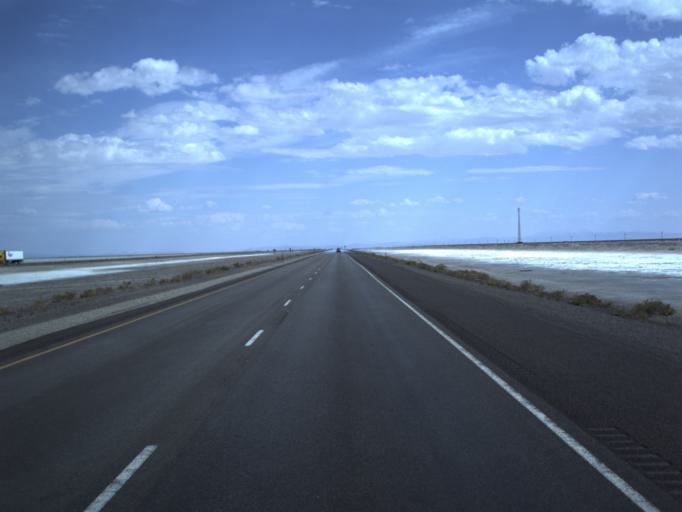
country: US
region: Utah
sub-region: Tooele County
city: Wendover
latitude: 40.7377
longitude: -113.8116
